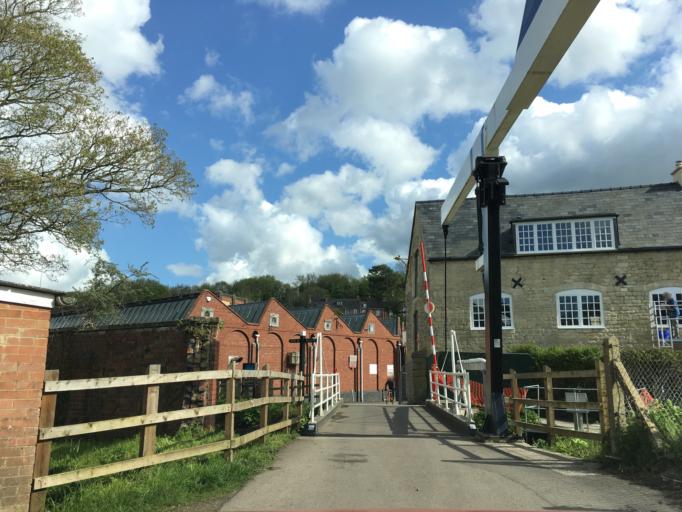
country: GB
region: England
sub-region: Gloucestershire
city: Stroud
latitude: 51.7441
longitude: -2.2283
